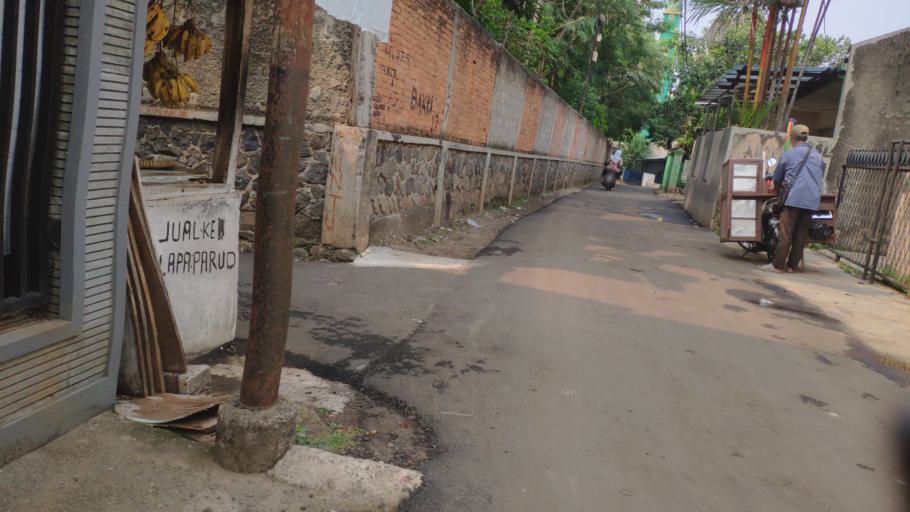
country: ID
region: West Java
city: Depok
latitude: -6.3461
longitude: 106.8078
